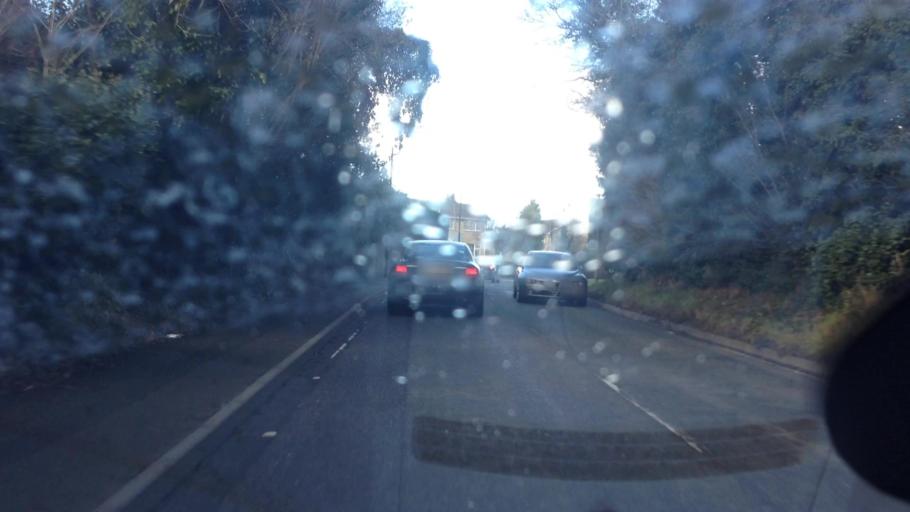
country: GB
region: England
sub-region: North Yorkshire
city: Knaresborough
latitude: 54.0008
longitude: -1.4501
